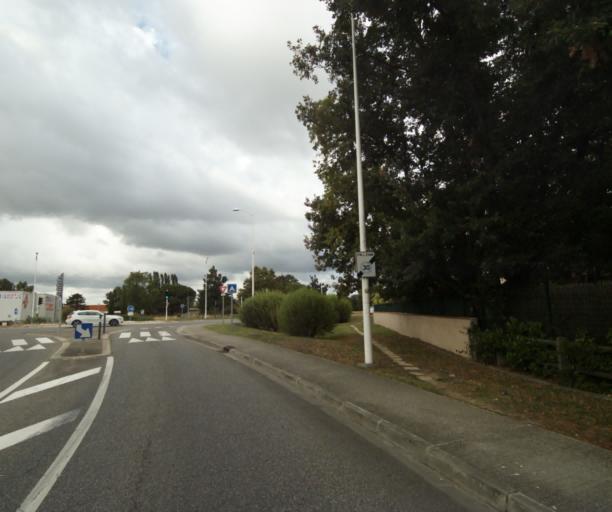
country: FR
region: Midi-Pyrenees
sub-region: Departement de la Haute-Garonne
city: Balma
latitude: 43.5934
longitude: 1.5057
